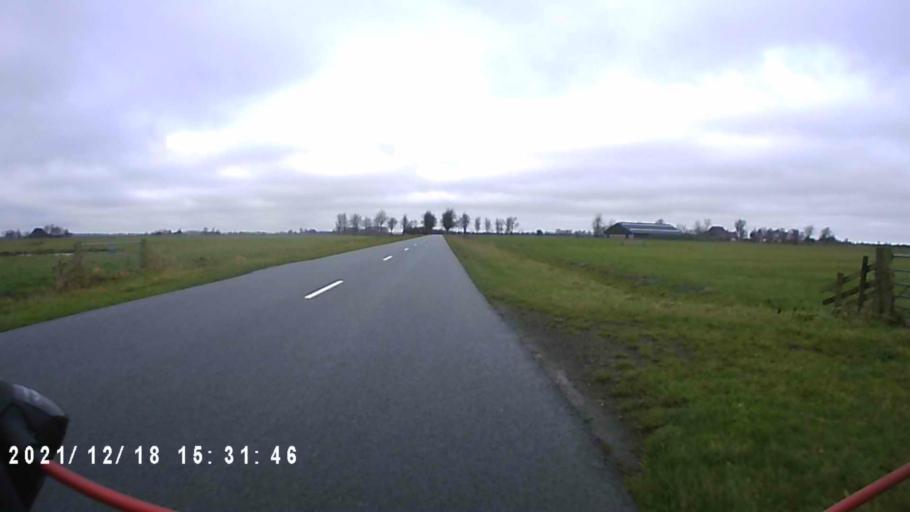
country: NL
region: Friesland
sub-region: Gemeente Dongeradeel
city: Anjum
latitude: 53.3402
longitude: 6.1361
